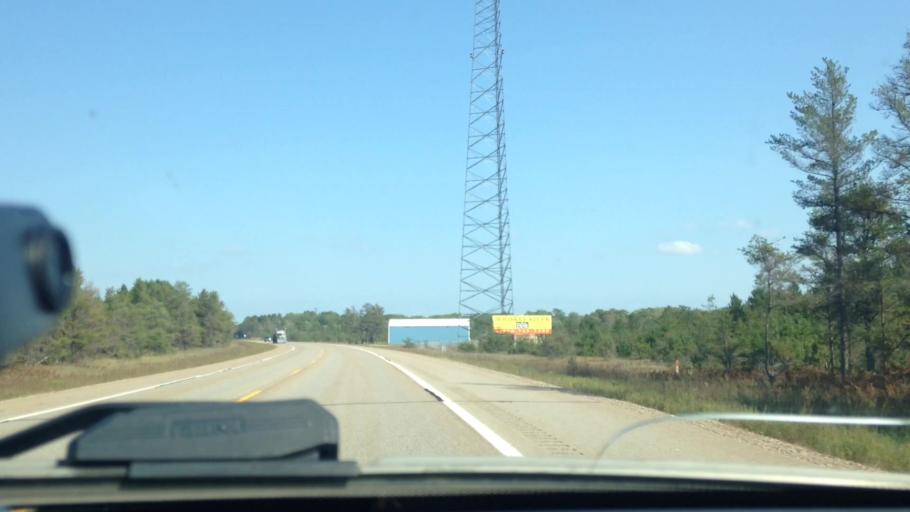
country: US
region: Michigan
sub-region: Chippewa County
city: Sault Ste. Marie
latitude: 46.3590
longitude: -84.7935
